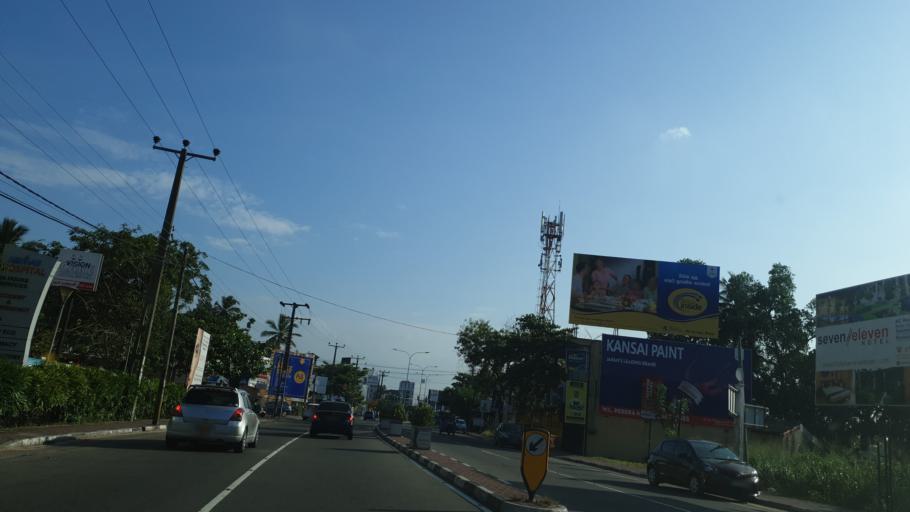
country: LK
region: Western
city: Battaramulla South
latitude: 6.8786
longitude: 79.9350
